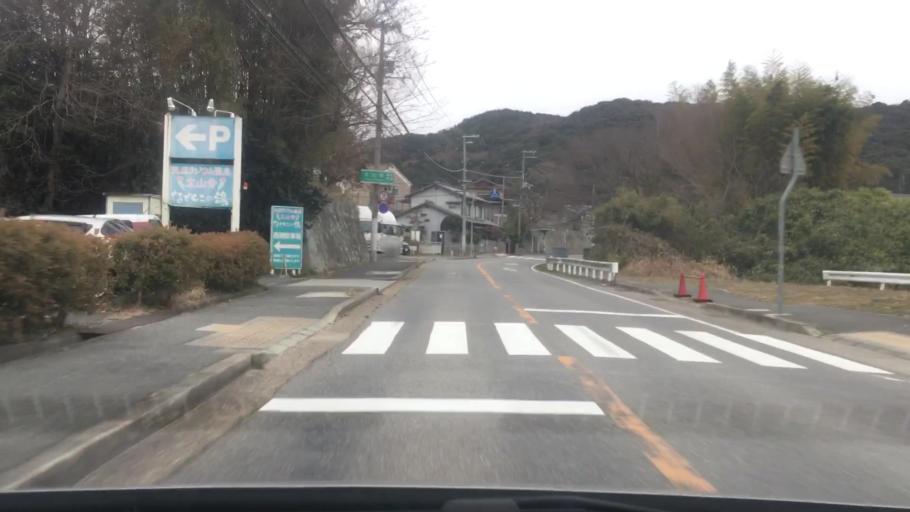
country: JP
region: Hyogo
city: Akashi
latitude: 34.6963
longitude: 135.0636
